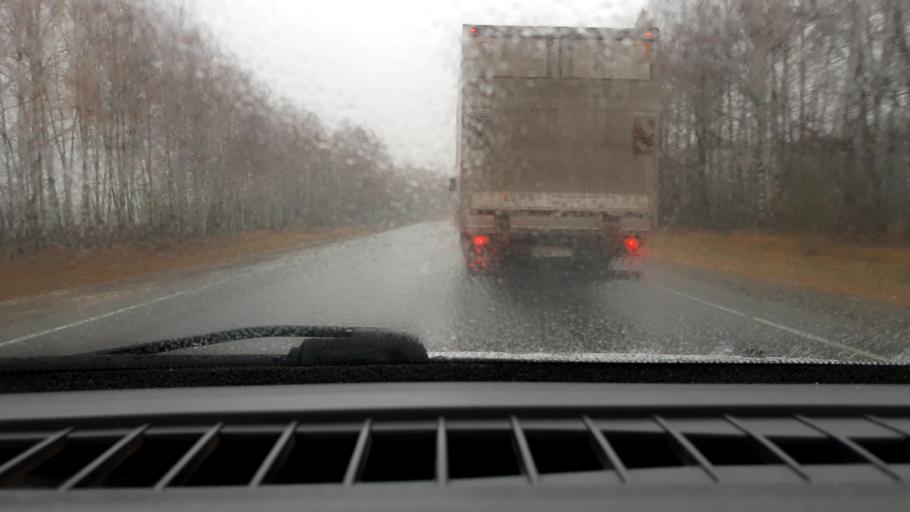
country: RU
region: Nizjnij Novgorod
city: Linda
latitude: 56.5604
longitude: 44.0246
